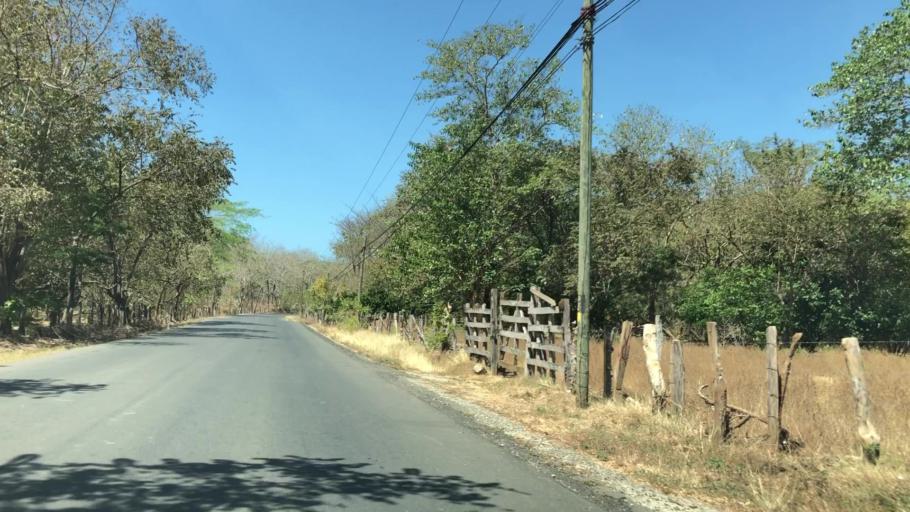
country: CR
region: Guanacaste
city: Sardinal
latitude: 10.3455
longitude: -85.8391
